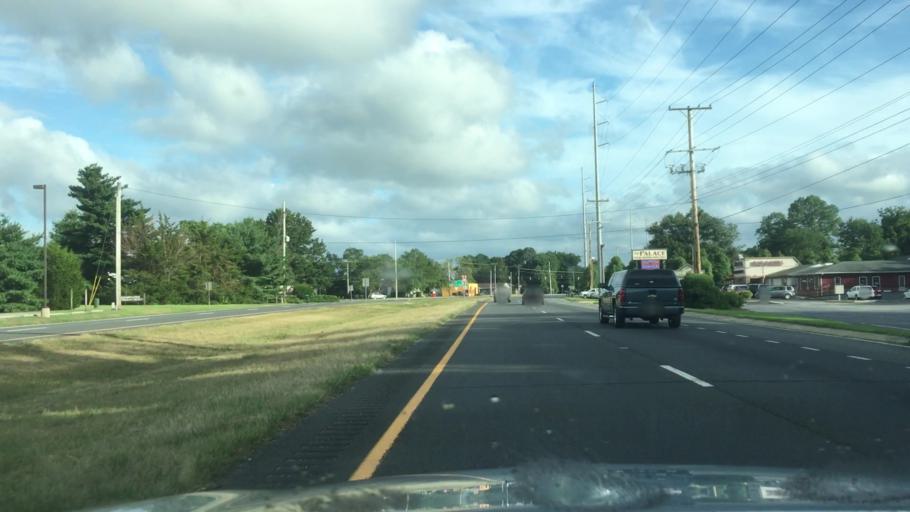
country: US
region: Delaware
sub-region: Sussex County
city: Milford
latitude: 38.9044
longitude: -75.4407
